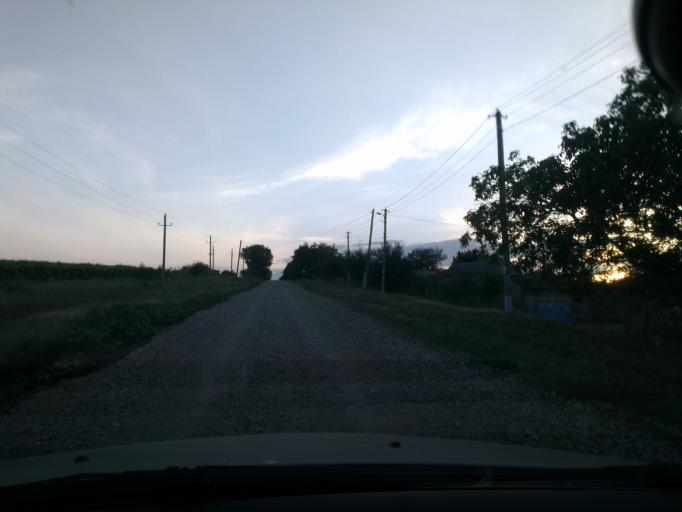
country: MD
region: Cantemir
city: Visniovca
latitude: 46.2863
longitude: 28.3845
